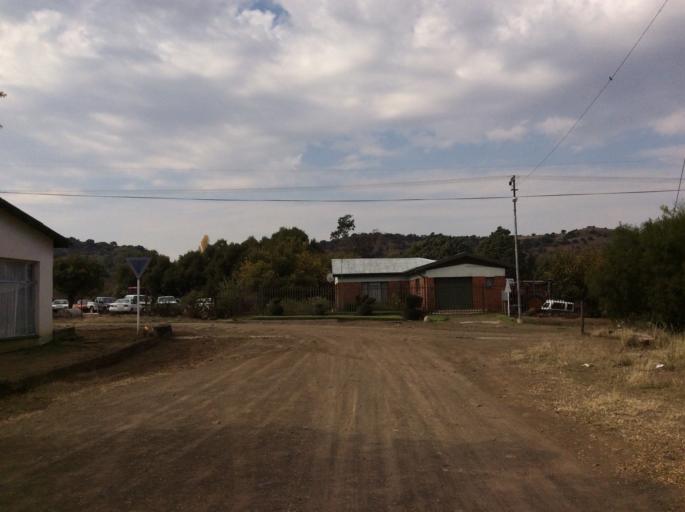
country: LS
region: Mafeteng
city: Mafeteng
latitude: -29.7256
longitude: 27.0430
